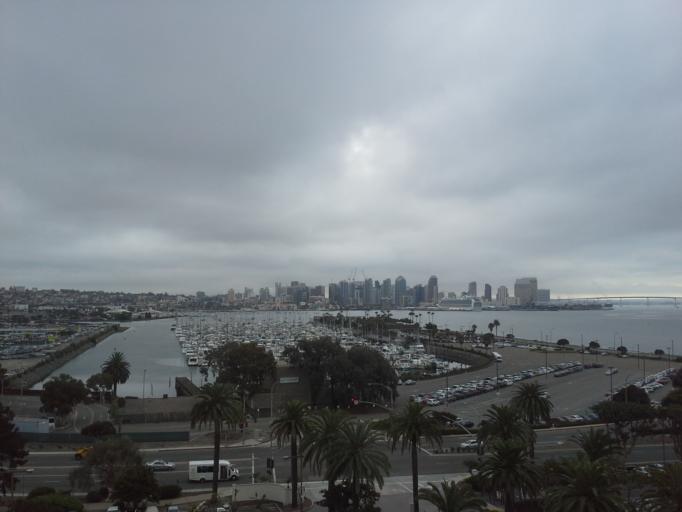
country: US
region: California
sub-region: San Diego County
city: San Diego
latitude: 32.7274
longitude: -117.1976
